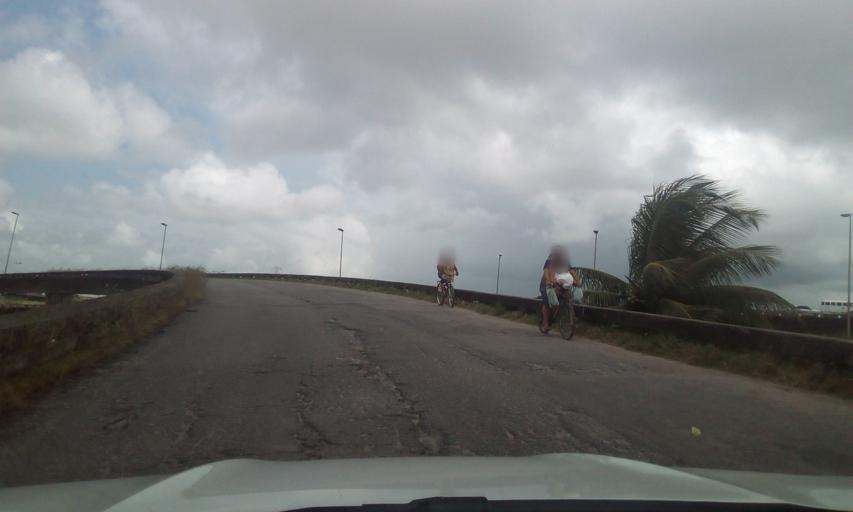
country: BR
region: Pernambuco
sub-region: Recife
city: Recife
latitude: -8.0646
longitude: -34.9428
